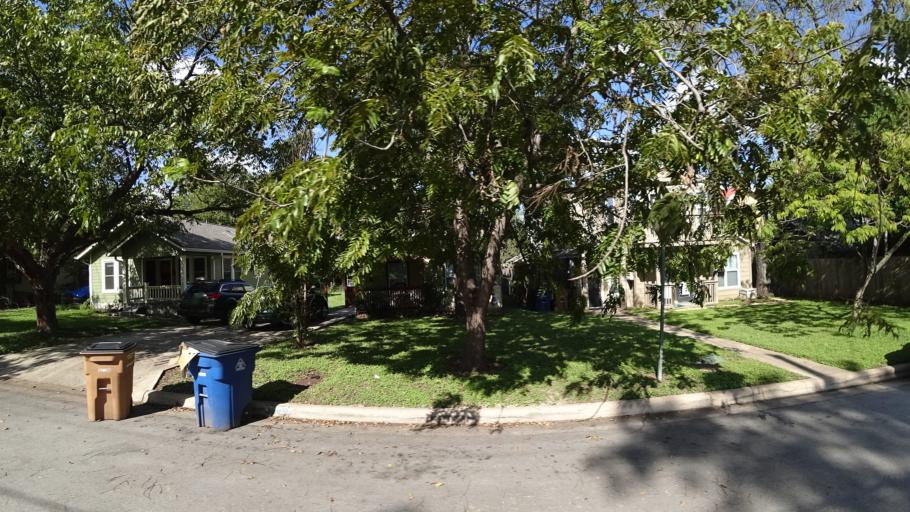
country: US
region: Texas
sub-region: Travis County
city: Austin
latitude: 30.3123
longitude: -97.7113
